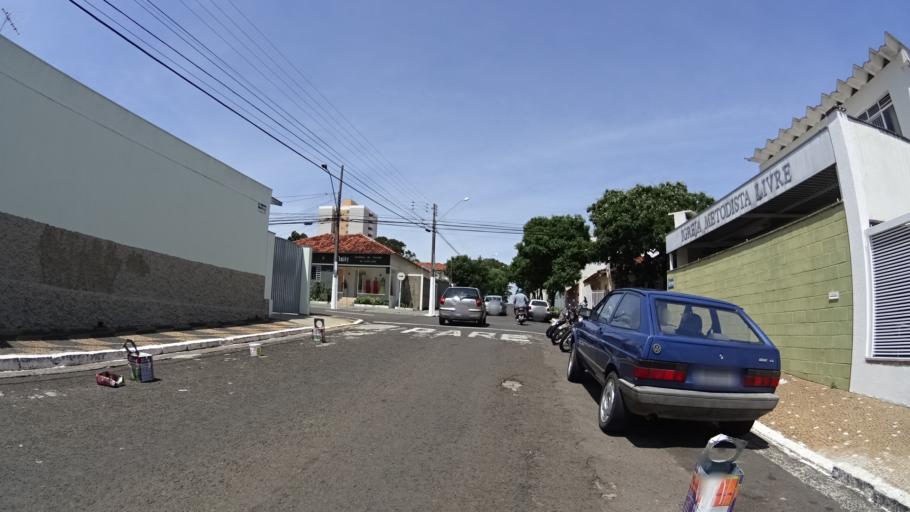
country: BR
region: Sao Paulo
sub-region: Marilia
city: Marilia
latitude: -22.2152
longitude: -49.9532
